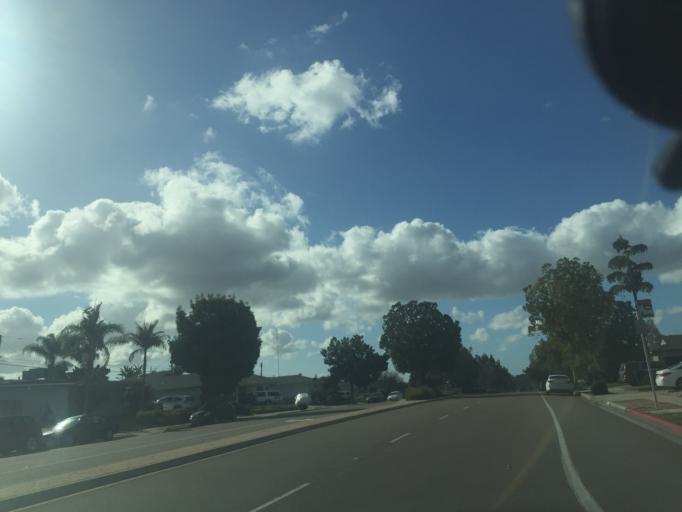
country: US
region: California
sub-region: San Diego County
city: La Mesa
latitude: 32.7950
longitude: -117.0785
